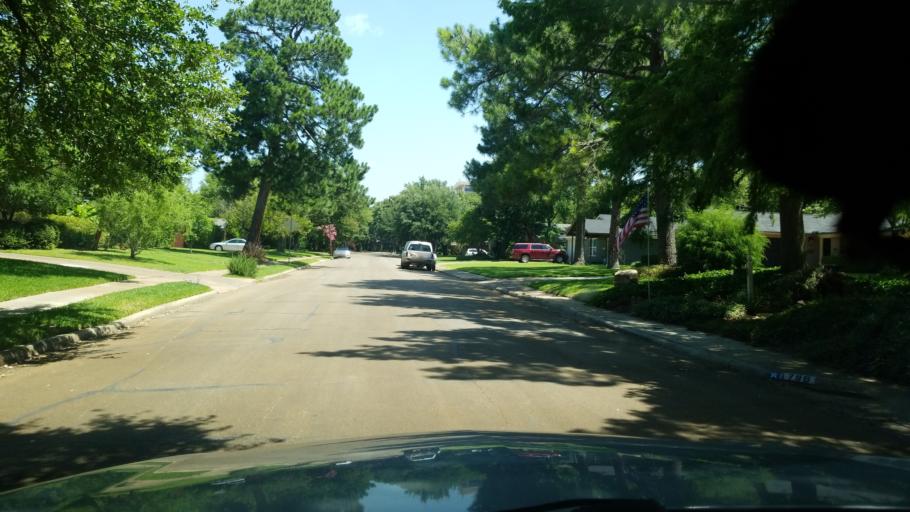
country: US
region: Texas
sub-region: Dallas County
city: Irving
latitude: 32.8320
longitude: -96.9553
